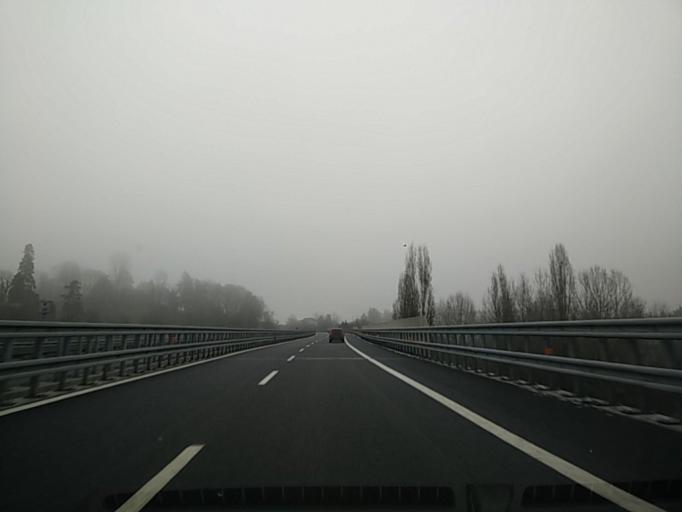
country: IT
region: Piedmont
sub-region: Provincia di Asti
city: Asti
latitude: 44.9167
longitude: 8.2077
